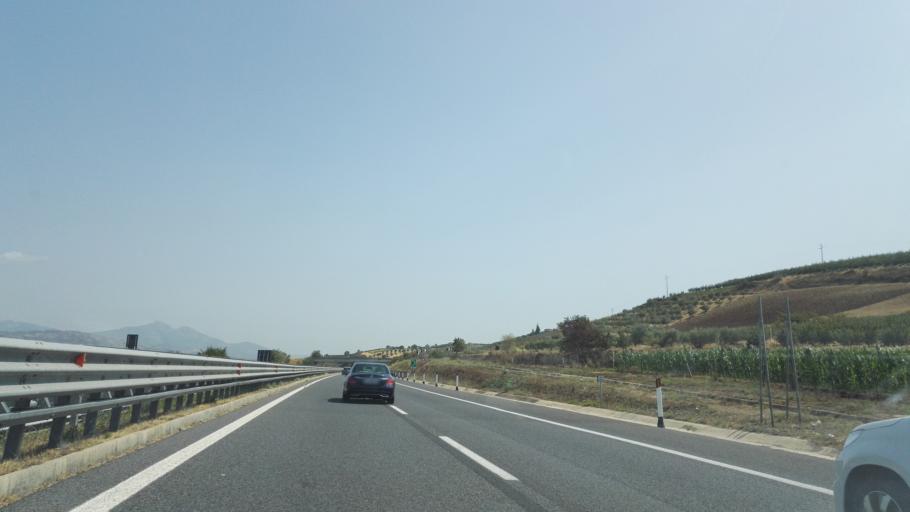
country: IT
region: Calabria
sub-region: Provincia di Cosenza
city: Firmo
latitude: 39.6869
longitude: 16.2263
